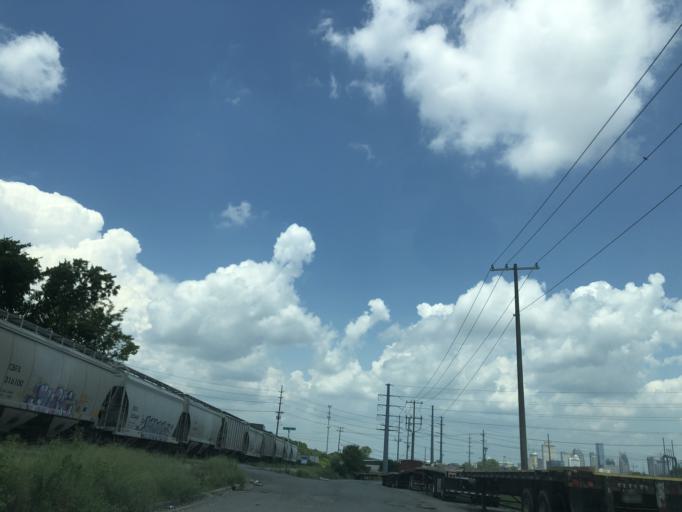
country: US
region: Tennessee
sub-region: Davidson County
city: Nashville
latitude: 36.1571
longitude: -86.8144
